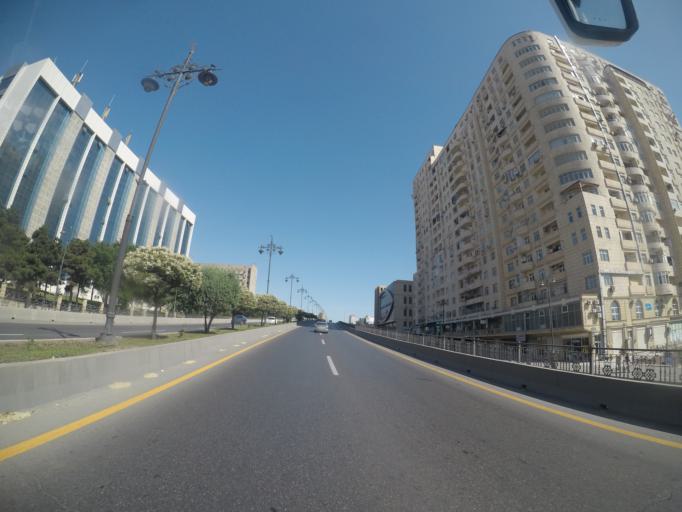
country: AZ
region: Baki
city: Khodzhi-Gasan
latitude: 40.4017
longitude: 49.8093
